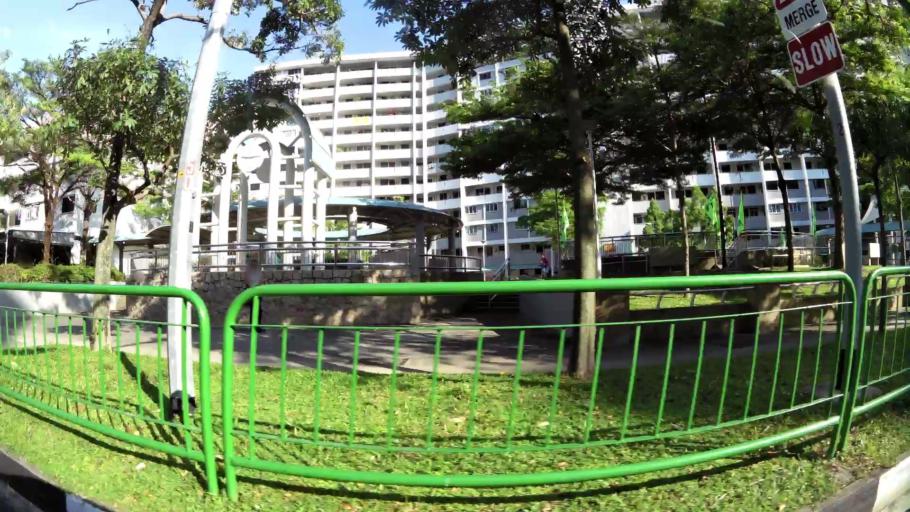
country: SG
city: Singapore
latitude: 1.3337
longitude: 103.9289
